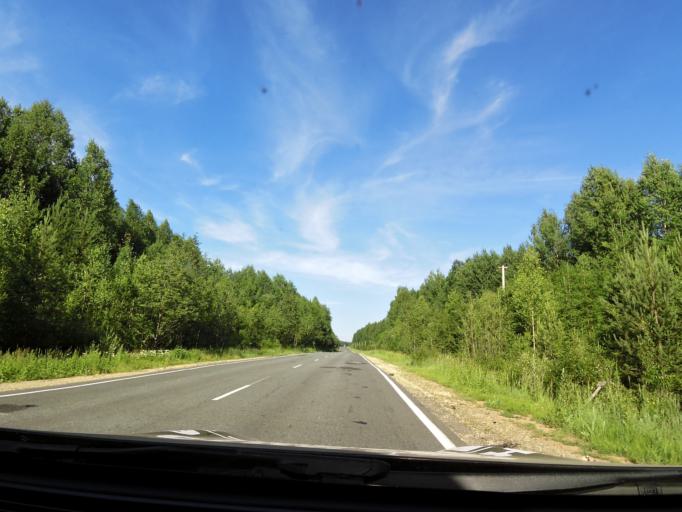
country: RU
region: Kirov
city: Belaya Kholunitsa
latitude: 58.9156
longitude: 51.0893
